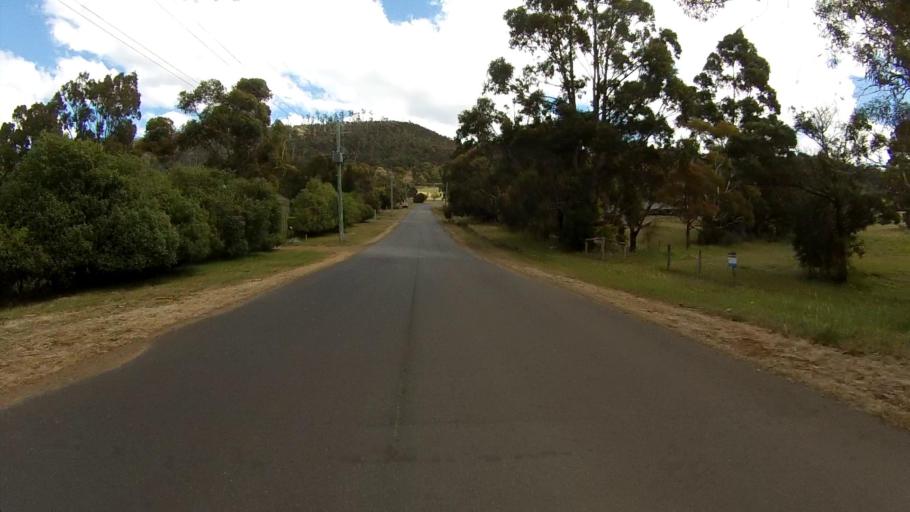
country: AU
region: Tasmania
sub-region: Clarence
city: Acton Park
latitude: -42.8850
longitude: 147.4789
